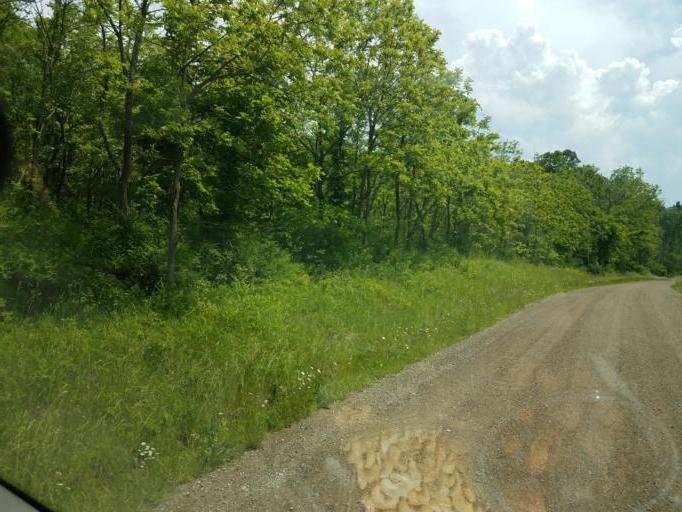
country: US
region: Ohio
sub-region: Knox County
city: Oak Hill
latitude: 40.3493
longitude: -82.2411
